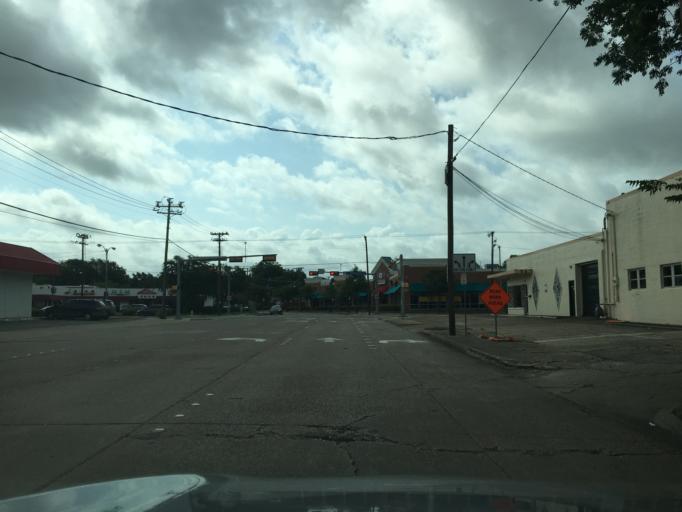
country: US
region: Texas
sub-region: Dallas County
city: Richardson
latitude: 32.9478
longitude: -96.7312
